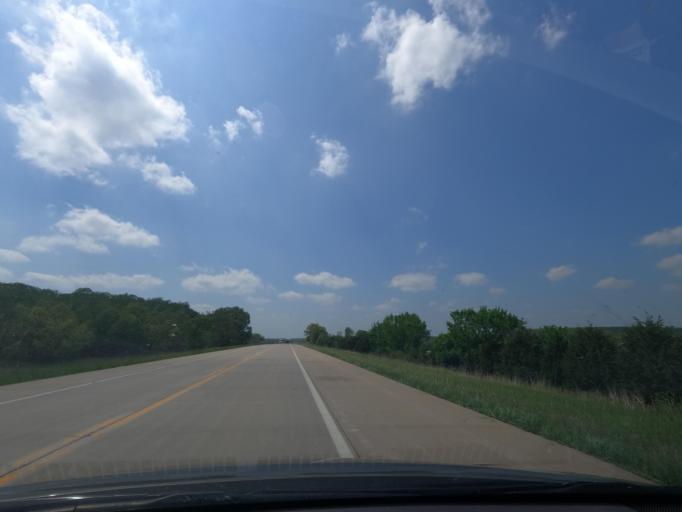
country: US
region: Kansas
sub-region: Wilson County
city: Fredonia
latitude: 37.6194
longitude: -95.9658
